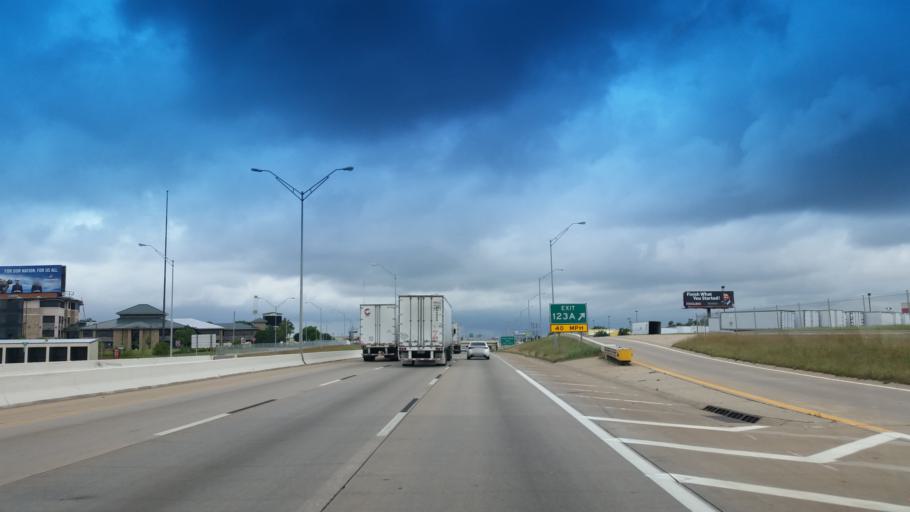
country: US
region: Oklahoma
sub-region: Oklahoma County
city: Del City
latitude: 35.4177
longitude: -97.4897
